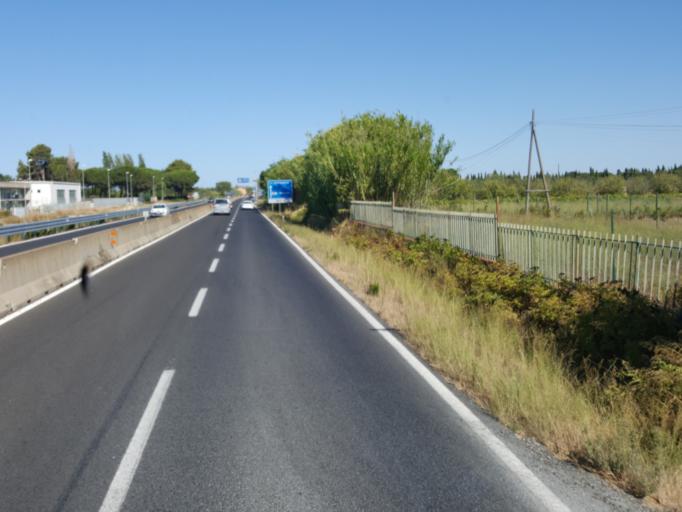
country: IT
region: Tuscany
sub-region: Provincia di Grosseto
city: Orbetello Scalo
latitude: 42.4663
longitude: 11.2405
